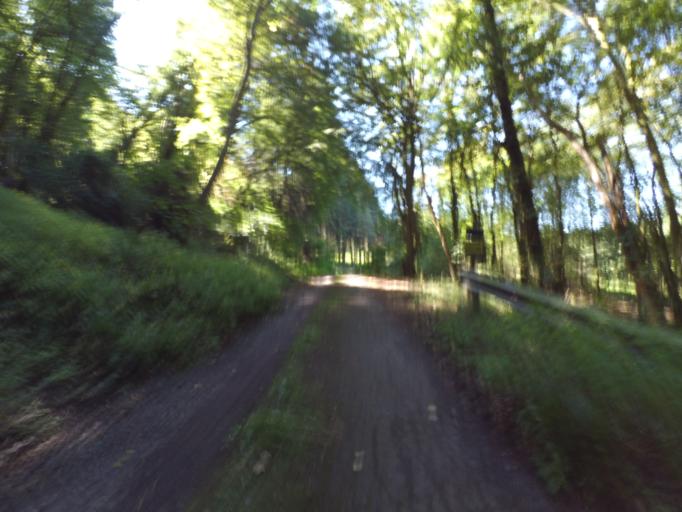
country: DE
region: Rheinland-Pfalz
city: Alf
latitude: 50.0612
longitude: 7.0975
